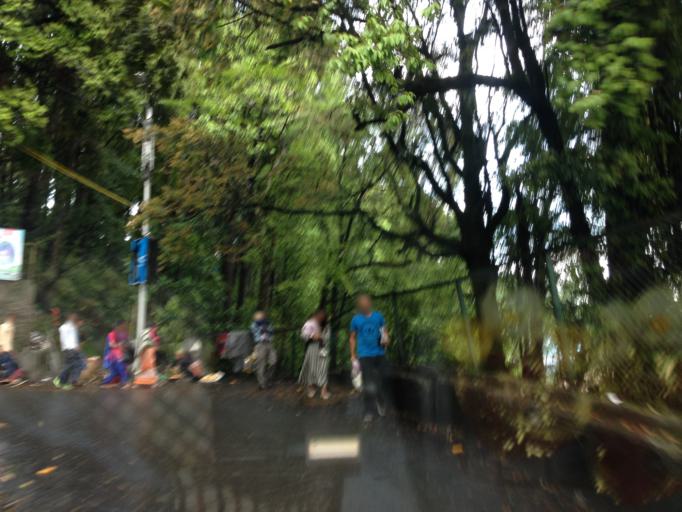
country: IN
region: West Bengal
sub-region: Darjiling
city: Darjiling
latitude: 27.0558
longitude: 88.2561
